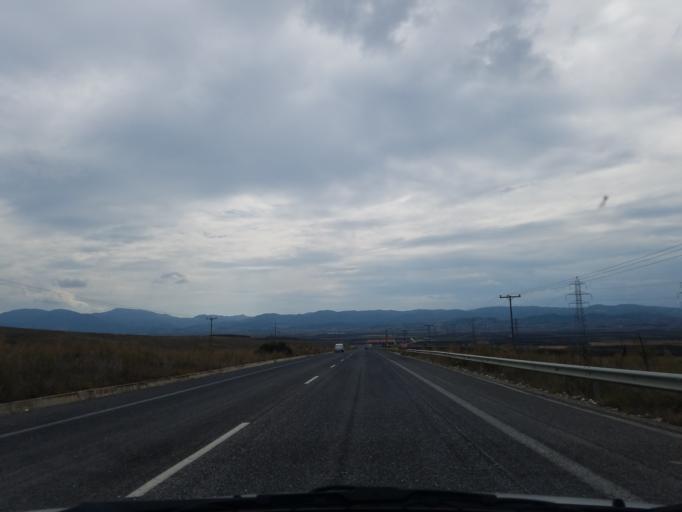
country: GR
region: Central Greece
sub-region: Nomos Fthiotidos
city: Omvriaki
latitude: 39.0912
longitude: 22.3056
